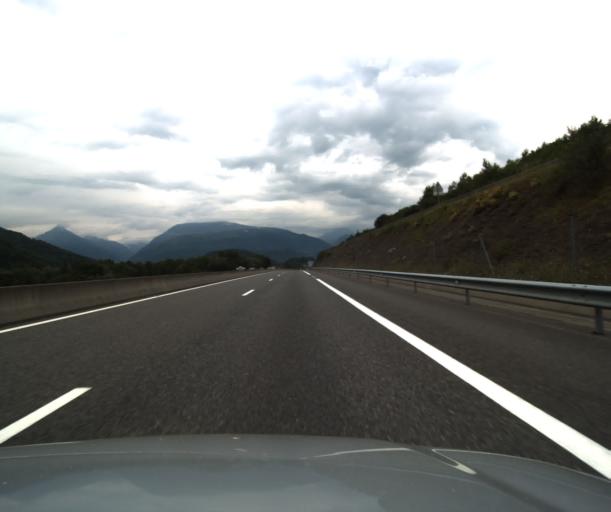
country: FR
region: Midi-Pyrenees
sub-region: Departement des Hautes-Pyrenees
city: Argeles-Gazost
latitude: 43.0451
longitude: -0.0607
